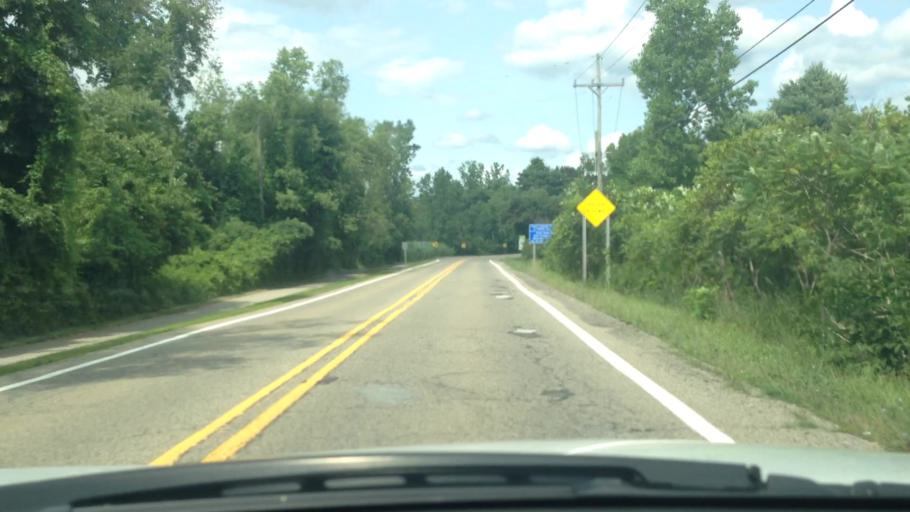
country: US
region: Michigan
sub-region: Oakland County
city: Clarkston
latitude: 42.7487
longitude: -83.3986
